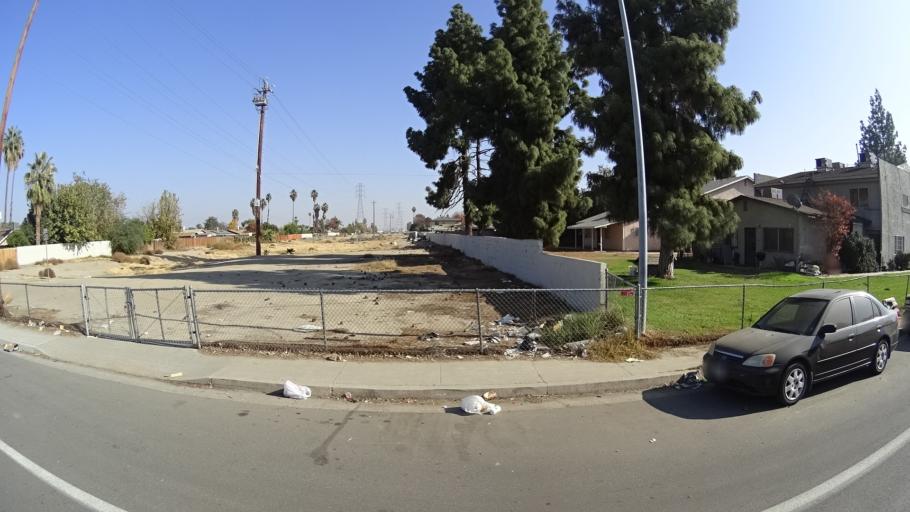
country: US
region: California
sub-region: Kern County
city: Greenfield
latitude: 35.3118
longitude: -119.0119
